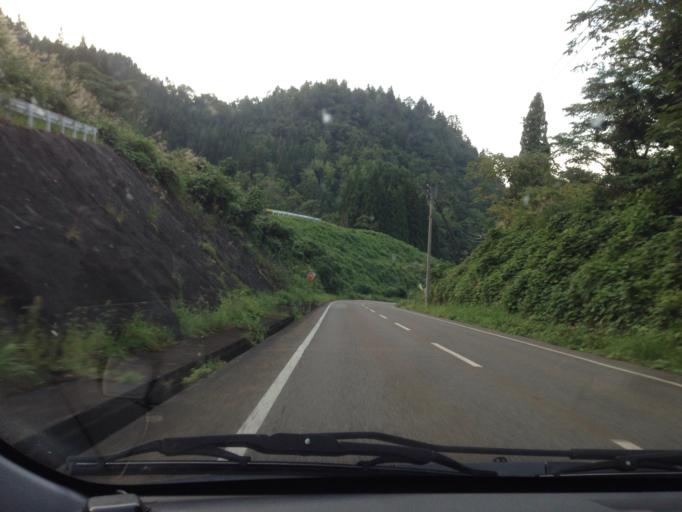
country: JP
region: Fukushima
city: Kitakata
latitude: 37.4775
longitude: 139.6902
